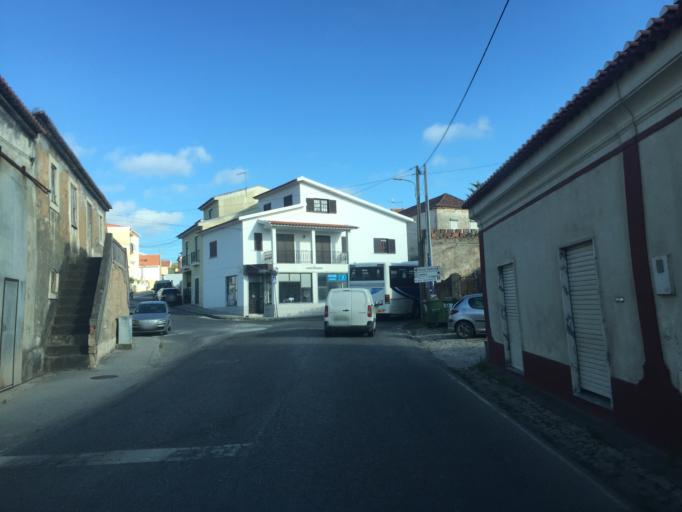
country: PT
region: Lisbon
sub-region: Torres Vedras
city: A dos Cunhados
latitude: 39.1532
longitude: -9.2982
